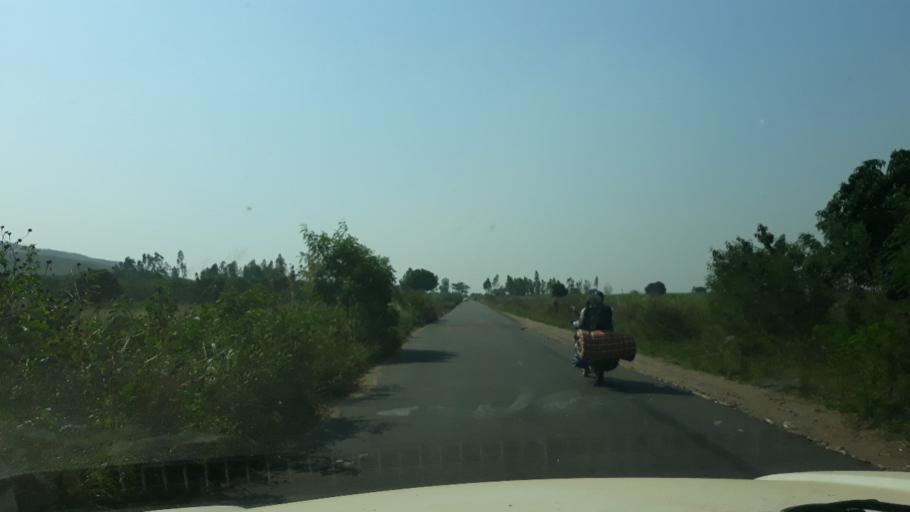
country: CD
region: South Kivu
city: Uvira
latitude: -3.2131
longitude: 29.1645
